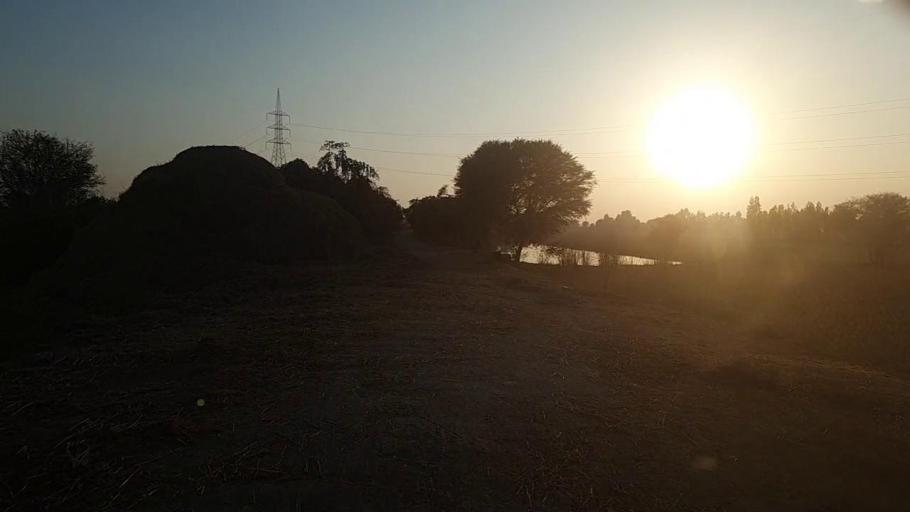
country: PK
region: Sindh
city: Mehar
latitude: 27.1864
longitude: 67.7404
